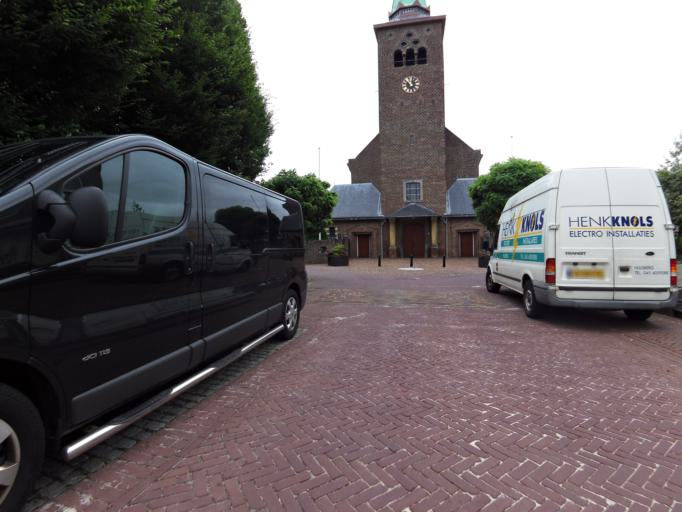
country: NL
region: Limburg
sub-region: Gemeente Voerendaal
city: Klimmen
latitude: 50.8896
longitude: 5.8604
